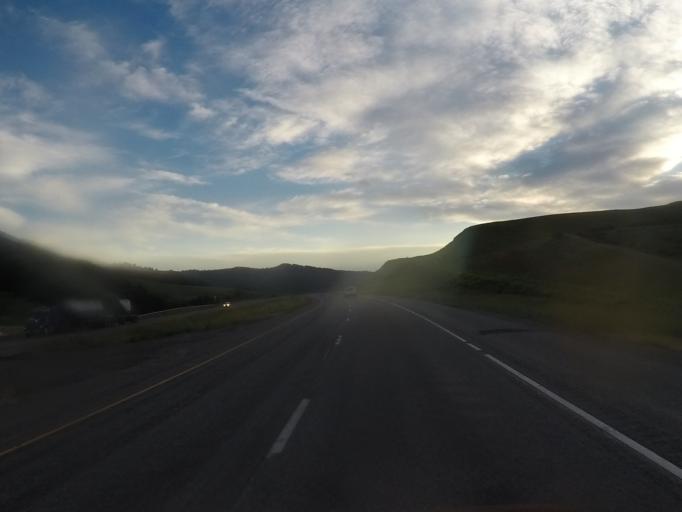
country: US
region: Montana
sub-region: Park County
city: Livingston
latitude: 45.6621
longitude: -110.7272
